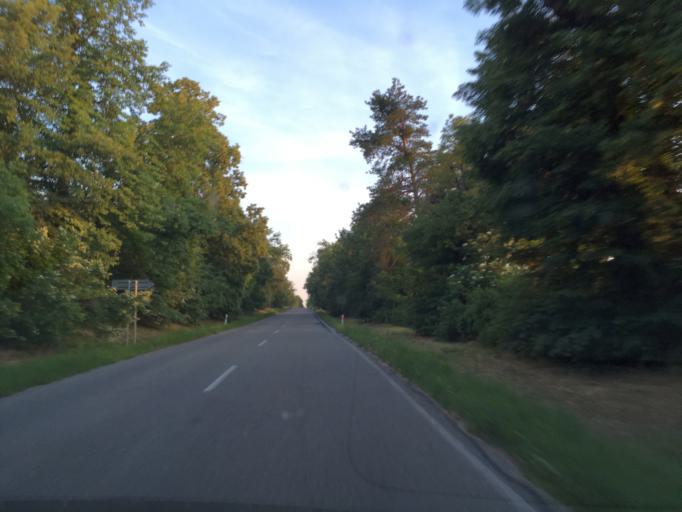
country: CZ
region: South Moravian
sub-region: Okres Breclav
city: Hlohovec
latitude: 48.7768
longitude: 16.7850
